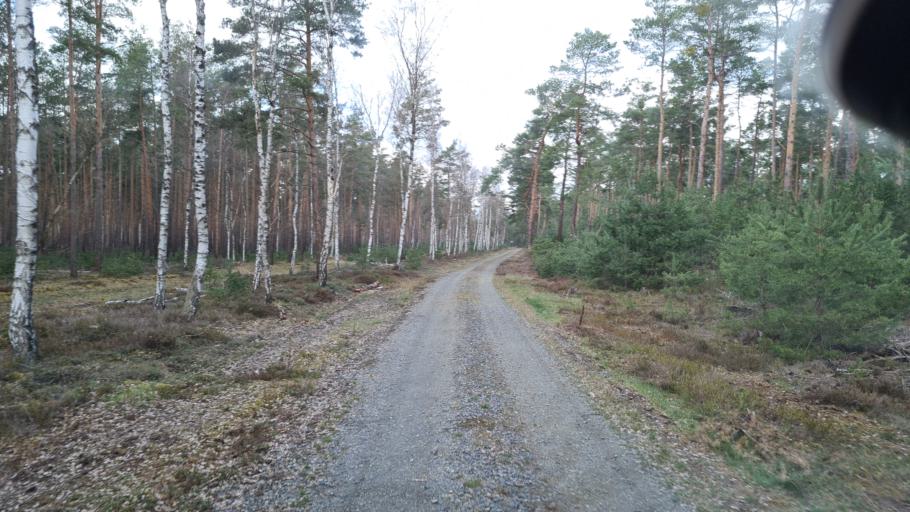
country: DE
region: Brandenburg
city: Schonborn
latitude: 51.6483
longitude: 13.4792
